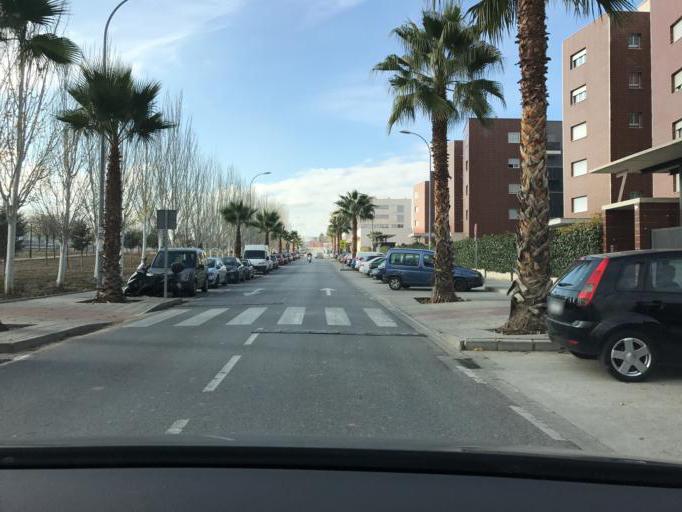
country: ES
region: Andalusia
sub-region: Provincia de Granada
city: Alhendin
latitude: 37.1064
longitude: -3.6375
